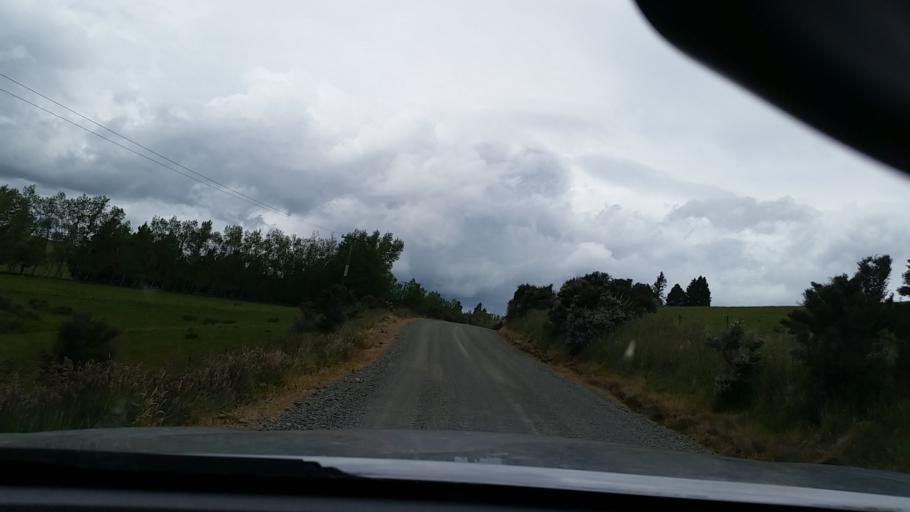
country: NZ
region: Southland
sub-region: Southland District
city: Winton
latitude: -45.8277
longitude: 168.1555
